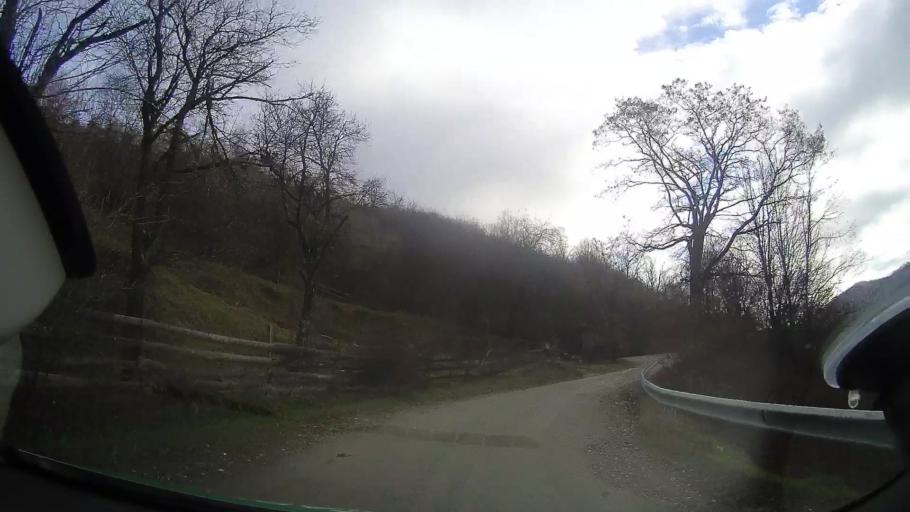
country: RO
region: Cluj
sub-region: Comuna Valea Ierii
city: Valea Ierii
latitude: 46.6469
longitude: 23.3485
